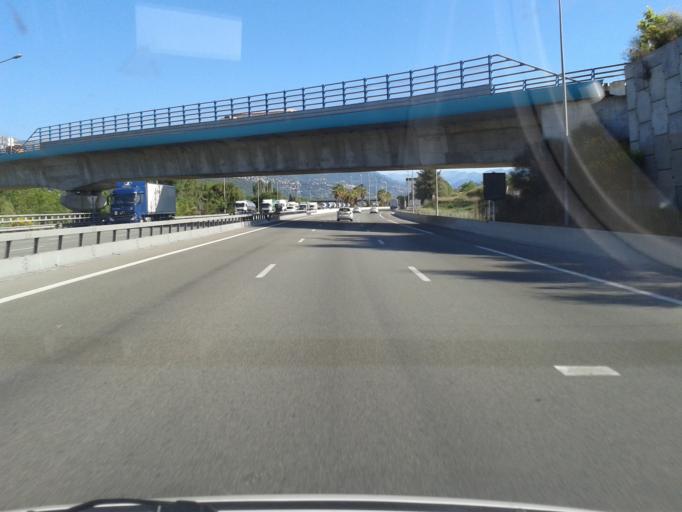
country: FR
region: Provence-Alpes-Cote d'Azur
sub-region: Departement des Alpes-Maritimes
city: Saint-Laurent-du-Var
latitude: 43.6958
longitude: 7.1890
